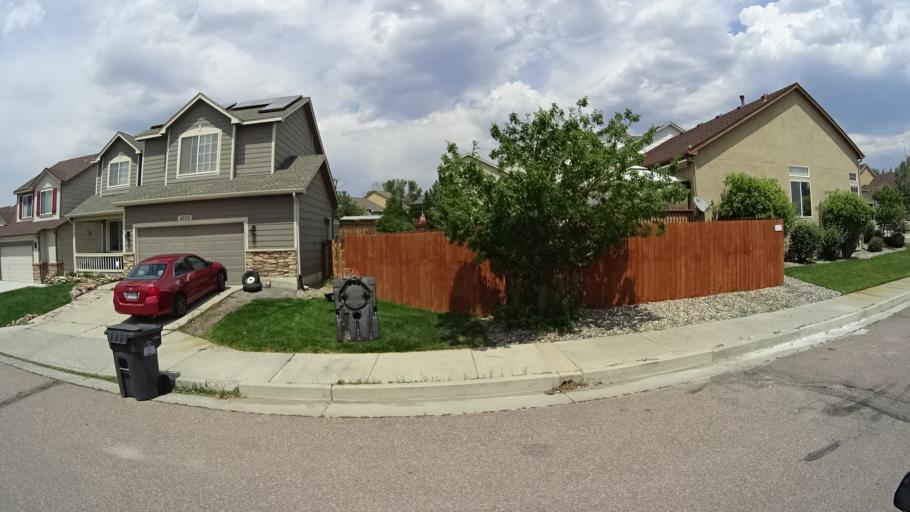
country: US
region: Colorado
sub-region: El Paso County
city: Black Forest
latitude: 38.9642
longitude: -104.7417
